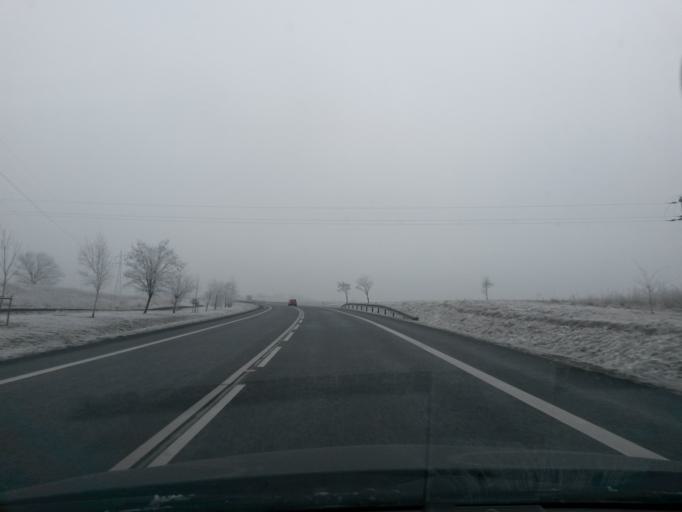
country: PL
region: Greater Poland Voivodeship
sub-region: Powiat gnieznienski
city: Gniezno
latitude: 52.5521
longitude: 17.6409
